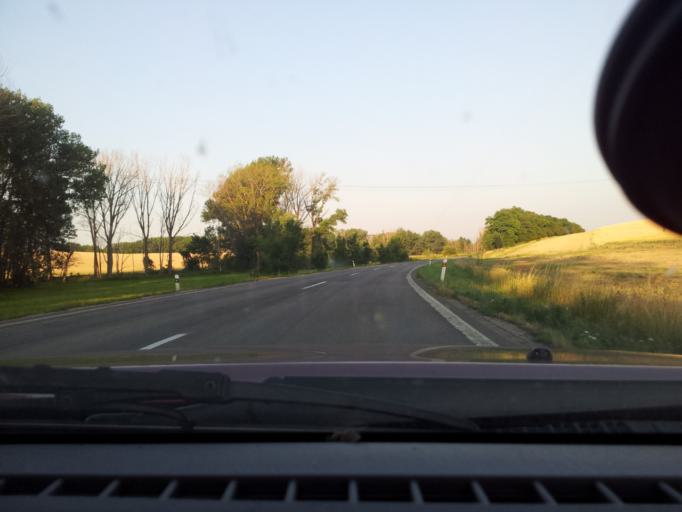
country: SK
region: Trnavsky
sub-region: Okres Skalica
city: Skalica
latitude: 48.7666
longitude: 17.2931
